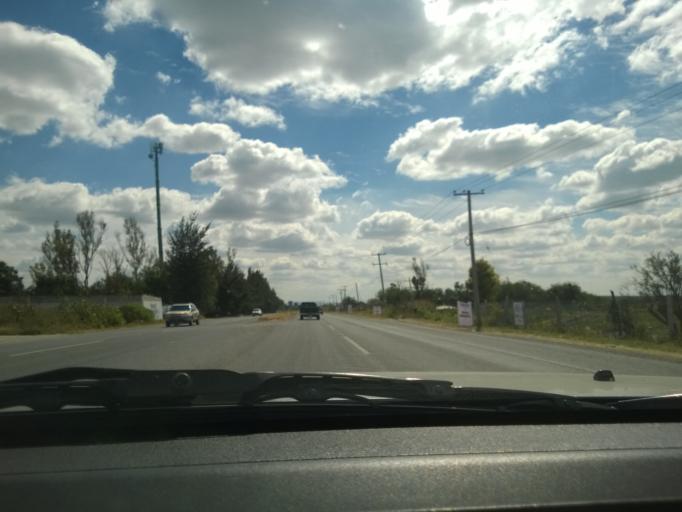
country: MX
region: Guanajuato
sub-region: Leon
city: El CERESO
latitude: 21.0200
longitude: -101.6986
